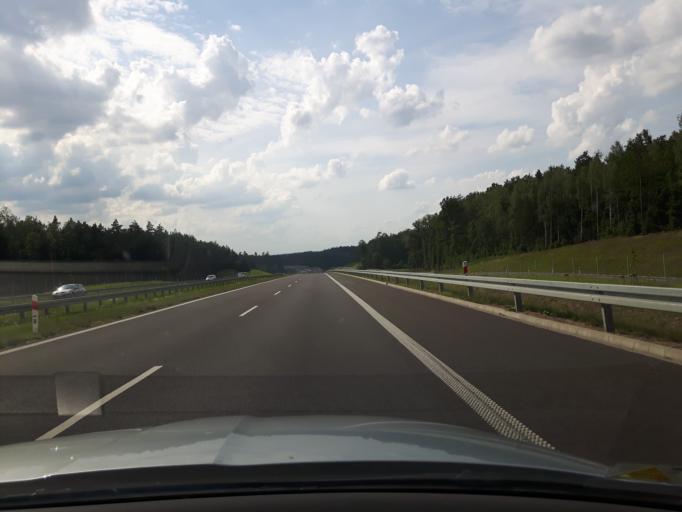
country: PL
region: Warmian-Masurian Voivodeship
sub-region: Powiat ostrodzki
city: Gierzwald
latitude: 53.5873
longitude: 20.1524
